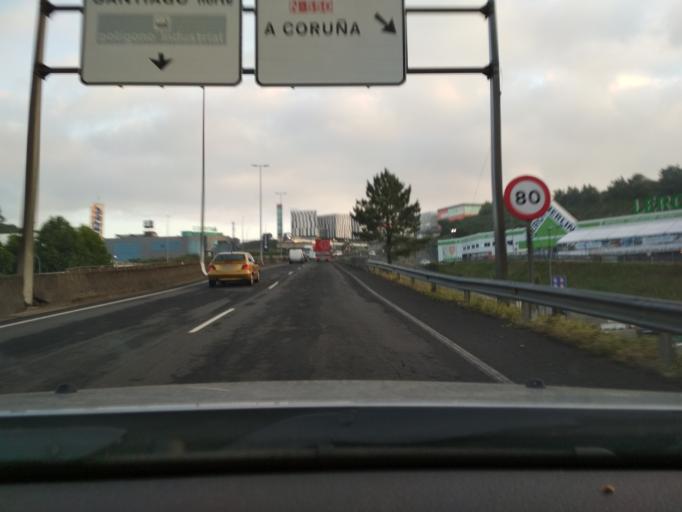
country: ES
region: Galicia
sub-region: Provincia da Coruna
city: Santiago de Compostela
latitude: 42.9019
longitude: -8.5113
